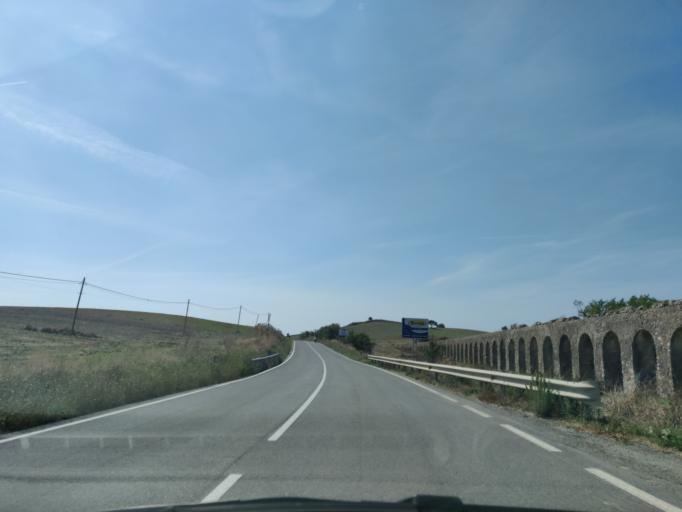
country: IT
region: Latium
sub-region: Provincia di Viterbo
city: Tarquinia
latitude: 42.2524
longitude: 11.8126
